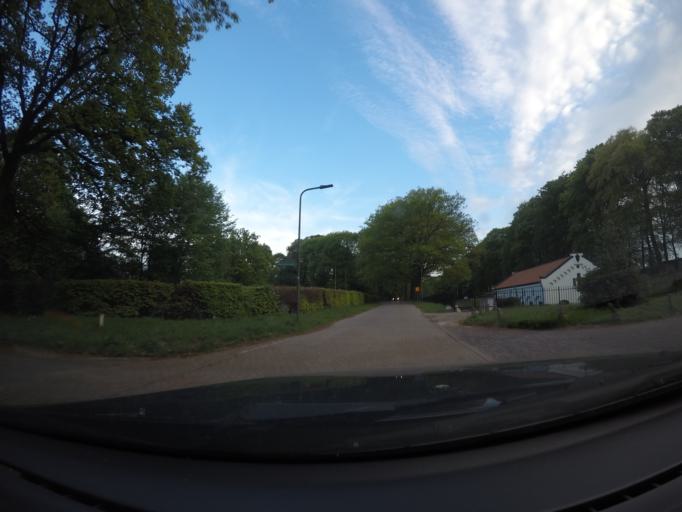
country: NL
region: Gelderland
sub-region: Gemeente Rheden
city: Velp
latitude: 52.0075
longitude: 5.9757
